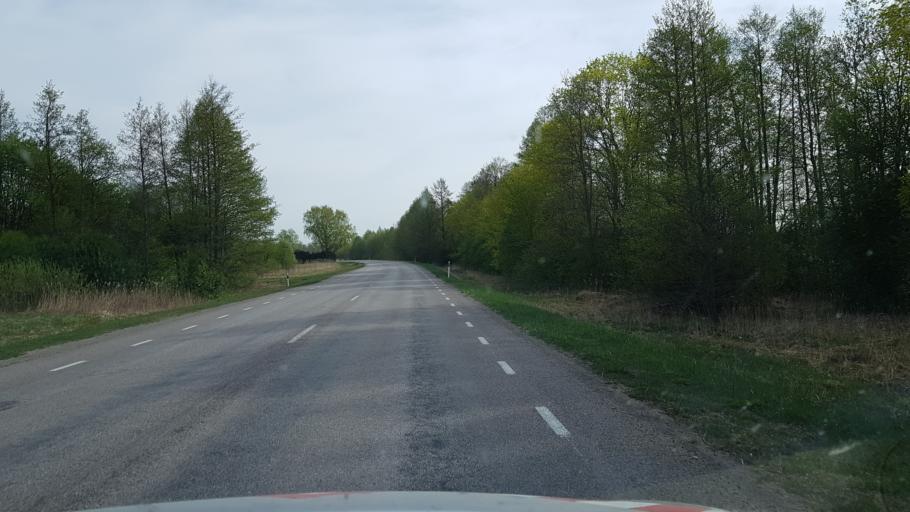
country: EE
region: Paernumaa
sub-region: Audru vald
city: Audru
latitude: 58.3992
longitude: 24.2951
